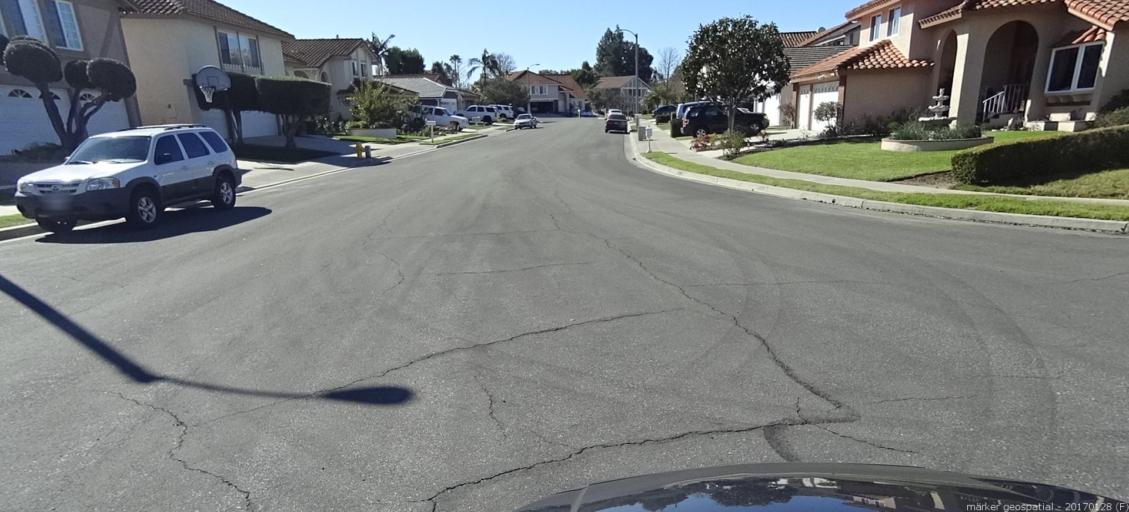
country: US
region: California
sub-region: Orange County
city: Lake Forest
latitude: 33.6579
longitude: -117.6941
